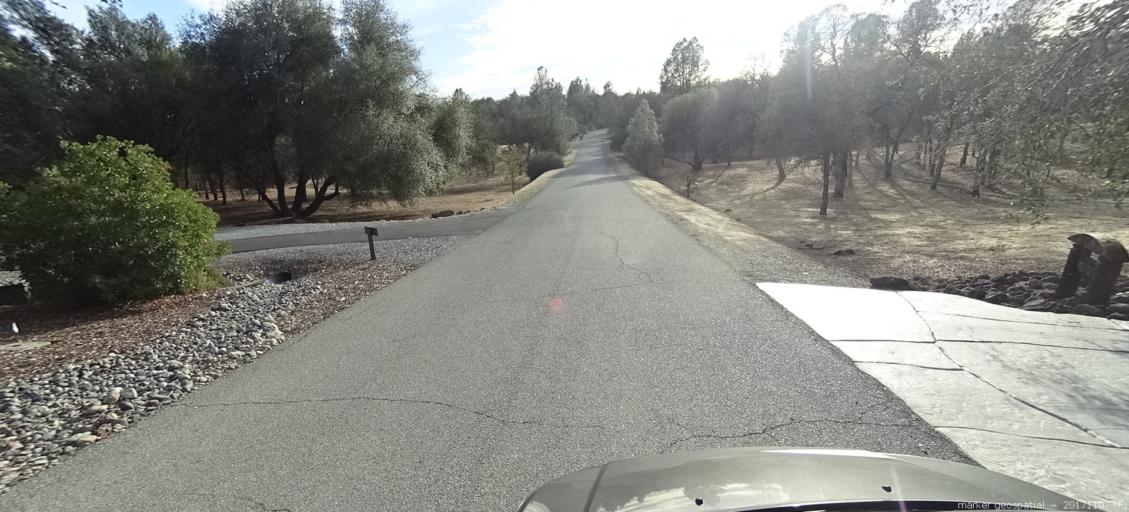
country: US
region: California
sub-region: Shasta County
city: Shasta
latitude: 40.5112
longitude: -122.4697
